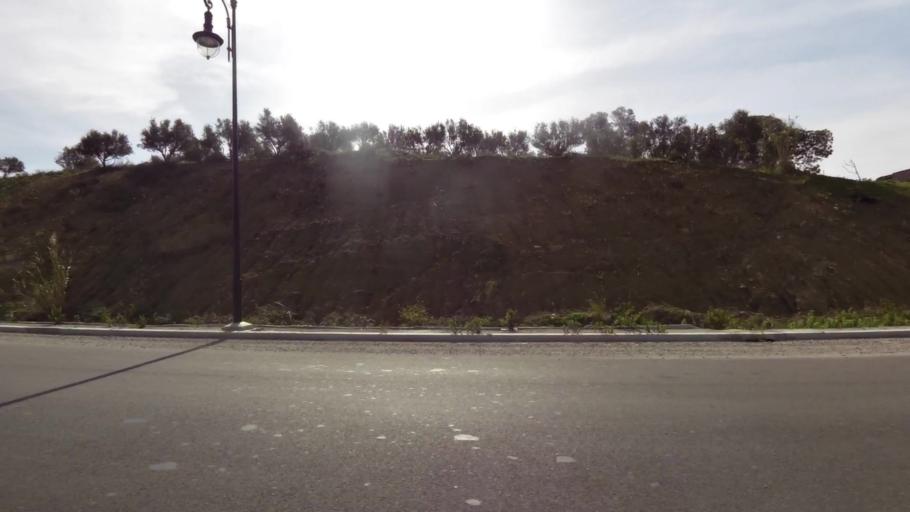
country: MA
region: Tanger-Tetouan
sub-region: Tanger-Assilah
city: Tangier
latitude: 35.7030
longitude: -5.7947
